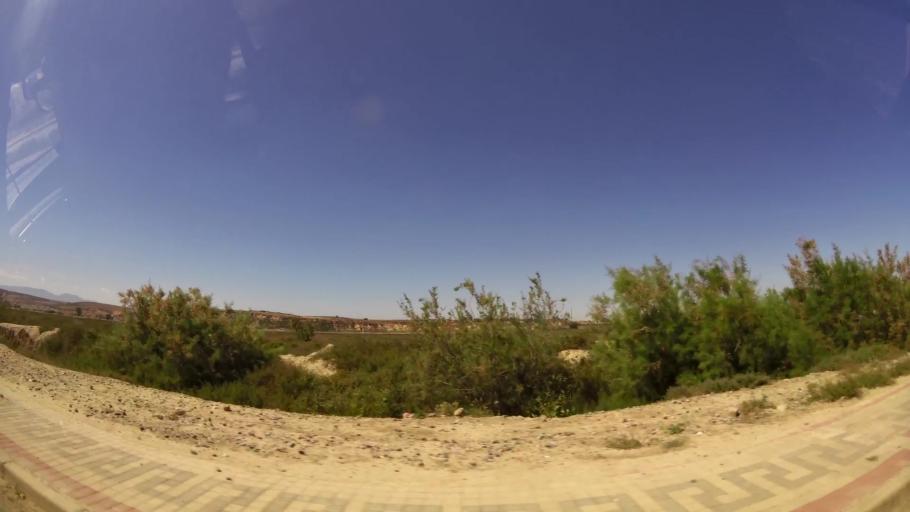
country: MA
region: Oriental
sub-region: Berkane-Taourirt
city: Madagh
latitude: 35.1052
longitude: -2.3163
